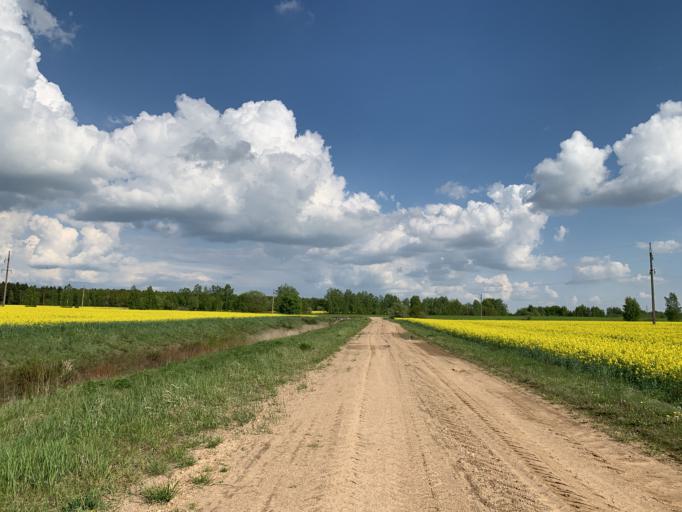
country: BY
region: Minsk
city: Kapyl'
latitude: 53.2422
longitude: 26.9557
